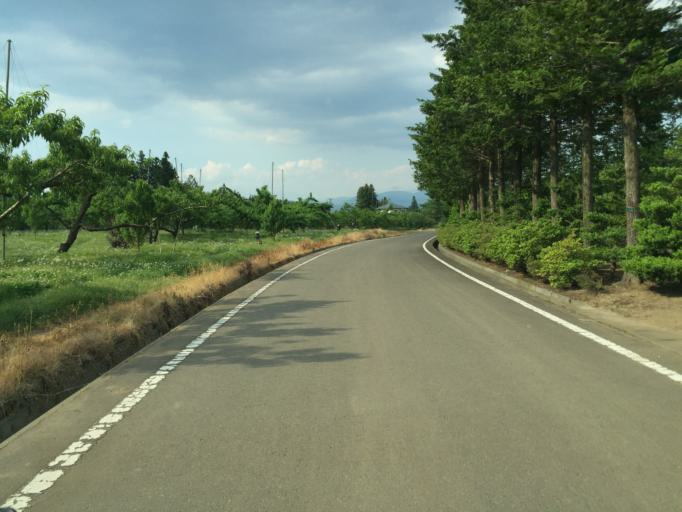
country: JP
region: Fukushima
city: Fukushima-shi
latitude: 37.7072
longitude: 140.3735
